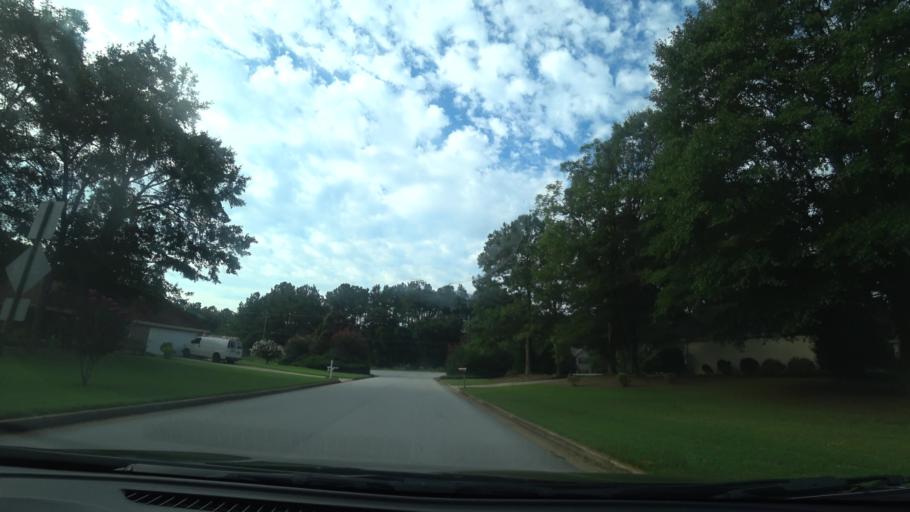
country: US
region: Georgia
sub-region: Newton County
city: Porterdale
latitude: 33.6130
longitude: -83.9488
